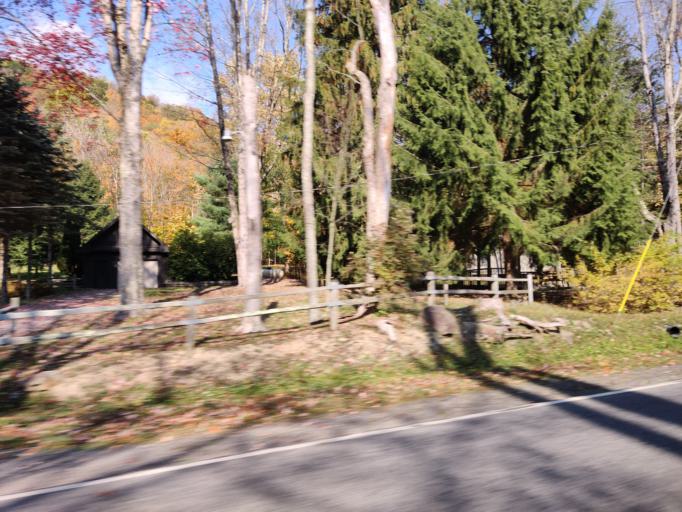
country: US
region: Pennsylvania
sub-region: Warren County
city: Sheffield
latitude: 41.6089
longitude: -79.0449
